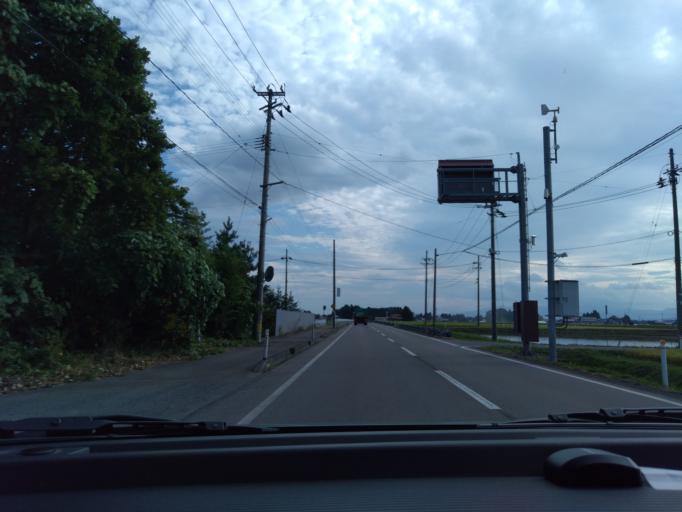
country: JP
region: Iwate
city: Hanamaki
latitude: 39.4420
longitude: 141.0984
